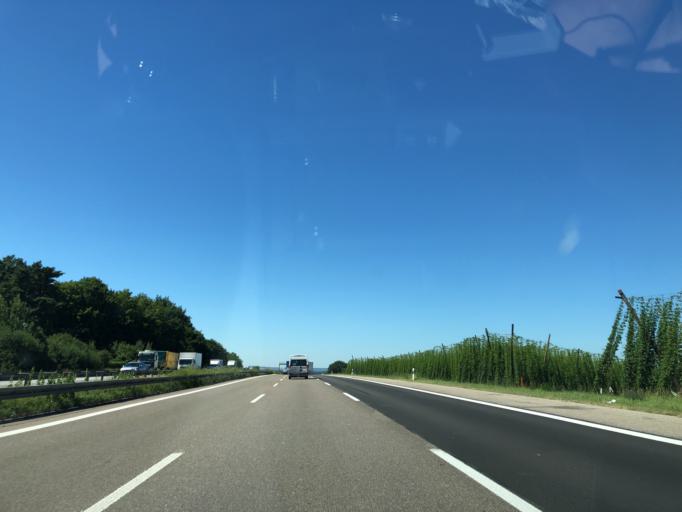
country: DE
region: Bavaria
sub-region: Upper Bavaria
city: Rohrbach
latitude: 48.6333
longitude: 11.5234
